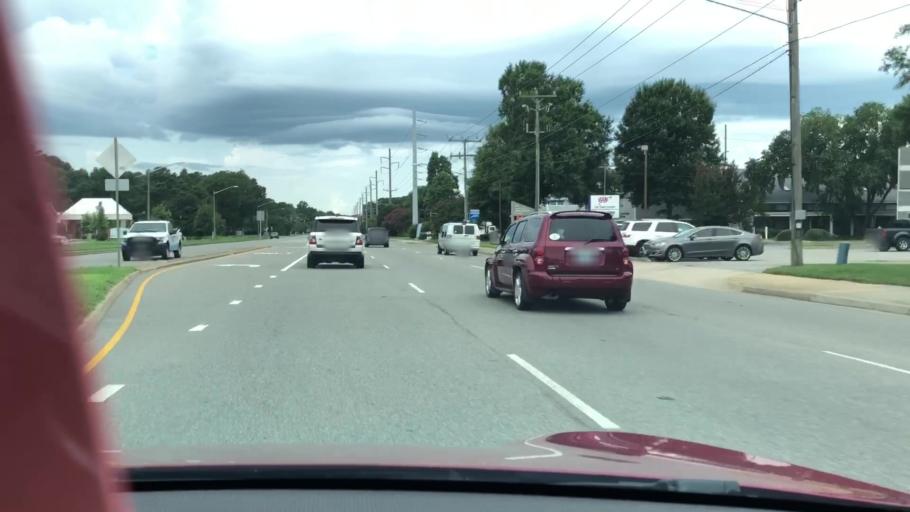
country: US
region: Virginia
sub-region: City of Virginia Beach
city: Virginia Beach
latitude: 36.8794
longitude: -76.0427
